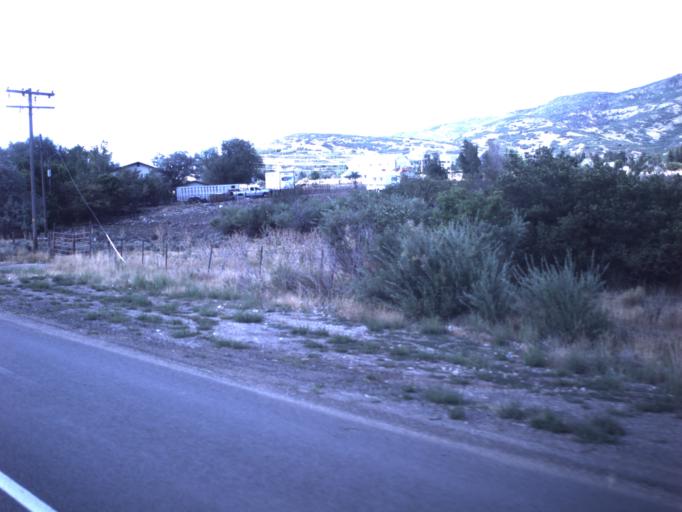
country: US
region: Utah
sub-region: Wasatch County
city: Heber
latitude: 40.5468
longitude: -111.4193
